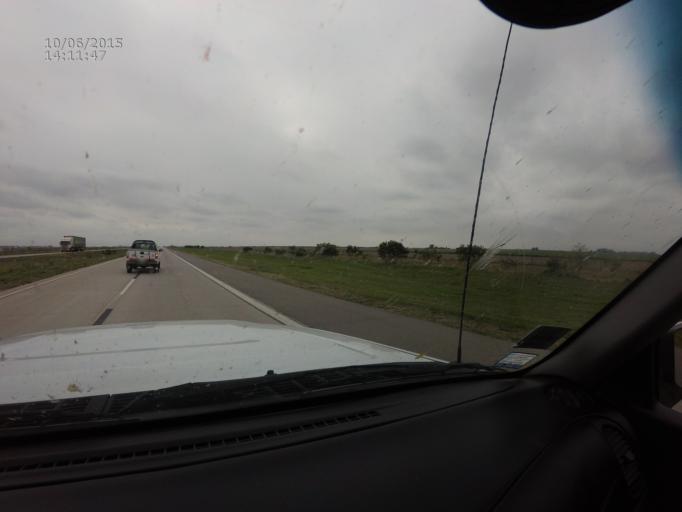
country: AR
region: Cordoba
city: Villa Maria
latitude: -32.4457
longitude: -63.1088
